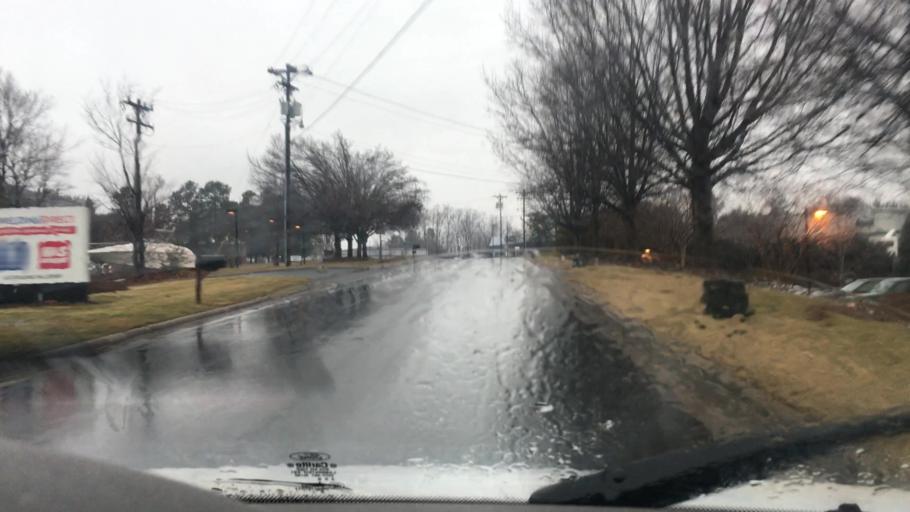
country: US
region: North Carolina
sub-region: Iredell County
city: Mooresville
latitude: 35.5833
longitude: -80.8605
